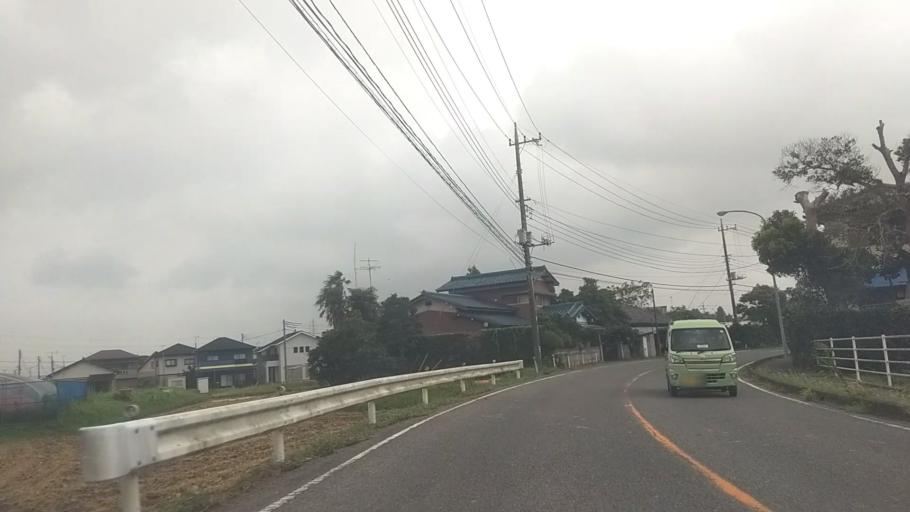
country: JP
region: Chiba
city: Ohara
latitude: 35.2826
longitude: 140.3034
